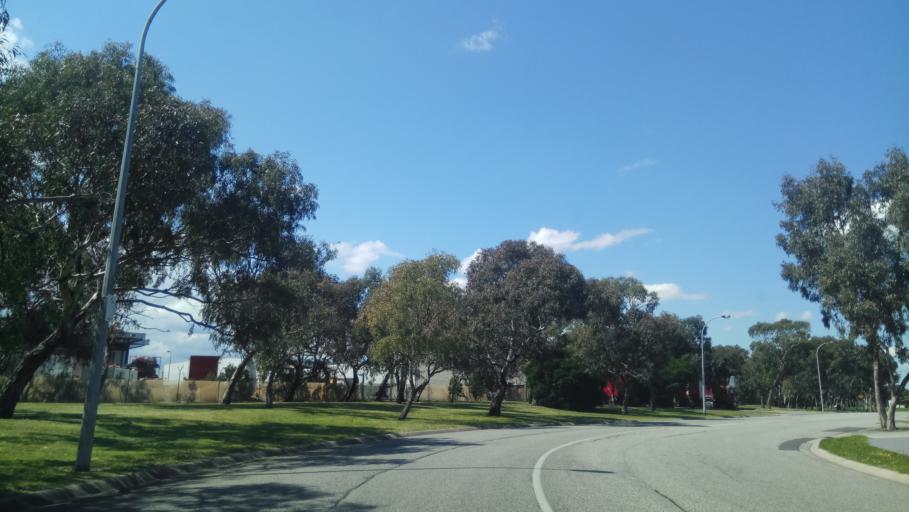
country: AU
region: Victoria
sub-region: Kingston
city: Waterways
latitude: -37.9986
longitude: 145.1166
